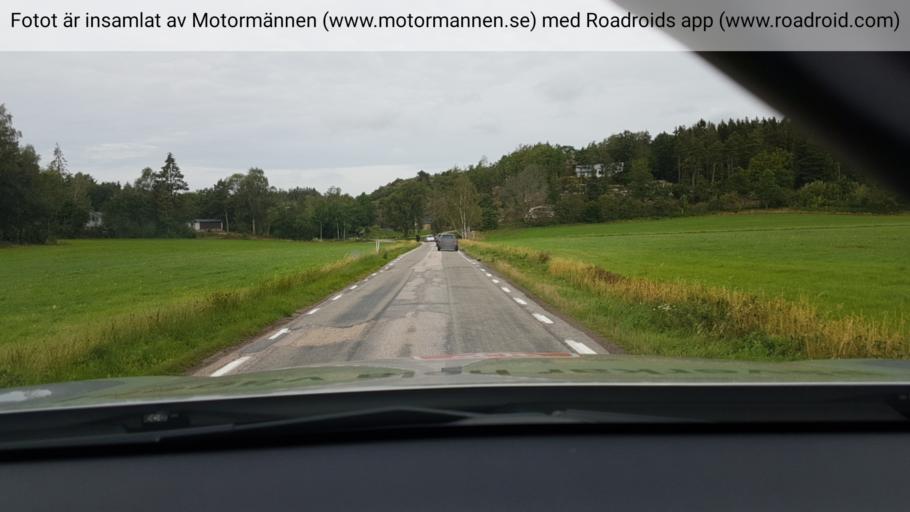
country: SE
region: Vaestra Goetaland
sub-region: Orust
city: Henan
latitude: 58.2469
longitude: 11.5547
